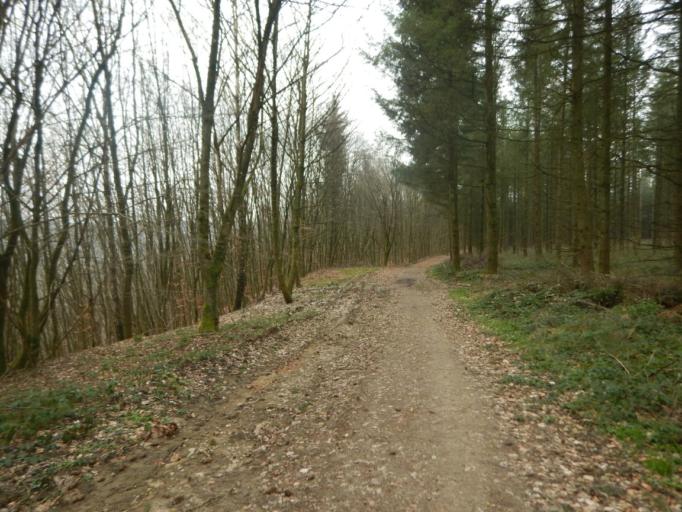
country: LU
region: Grevenmacher
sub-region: Canton d'Echternach
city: Beaufort
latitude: 49.8372
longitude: 6.3167
